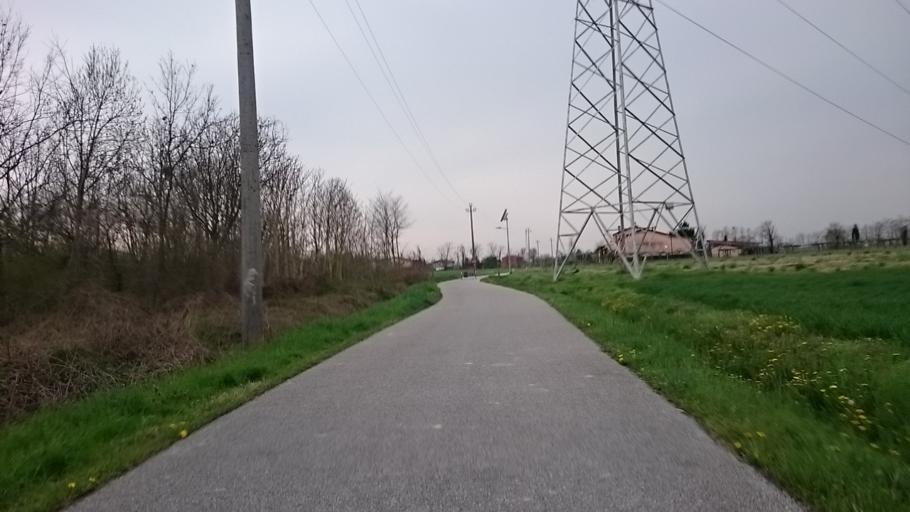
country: IT
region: Veneto
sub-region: Provincia di Padova
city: Tremignon
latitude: 45.5130
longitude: 11.8219
